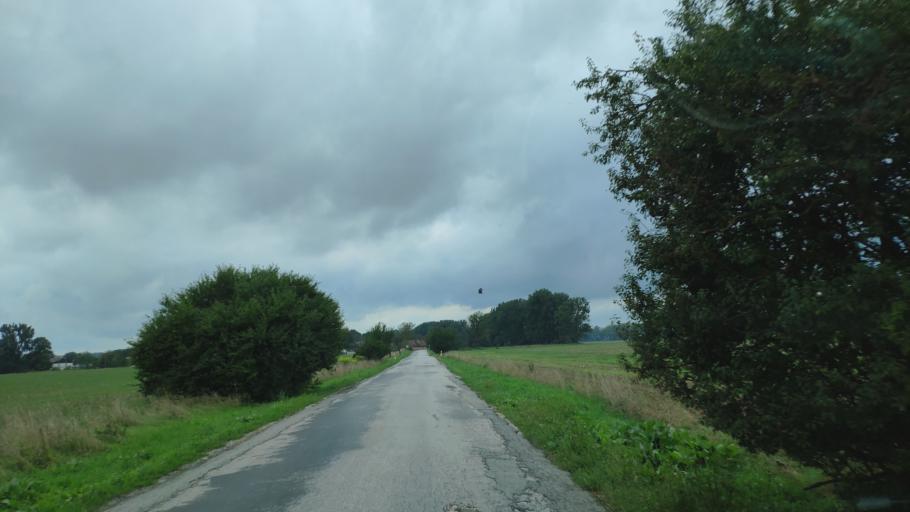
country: SK
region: Kosicky
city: Moldava nad Bodvou
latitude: 48.5845
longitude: 20.8919
